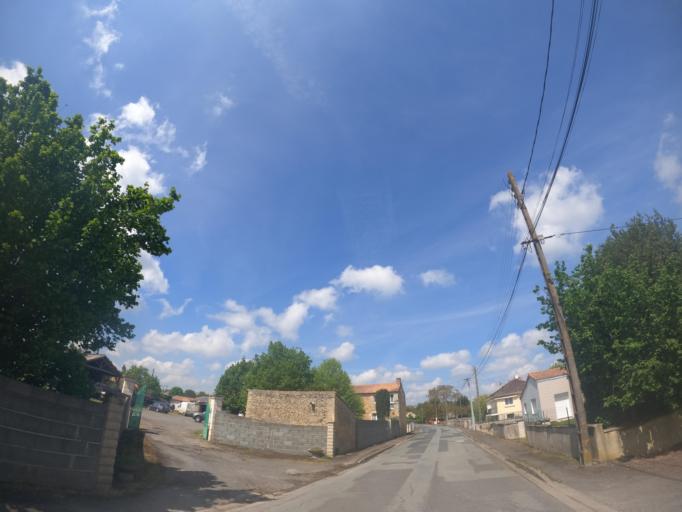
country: FR
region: Poitou-Charentes
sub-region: Departement des Deux-Sevres
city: Saint-Varent
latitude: 46.8566
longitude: -0.1997
